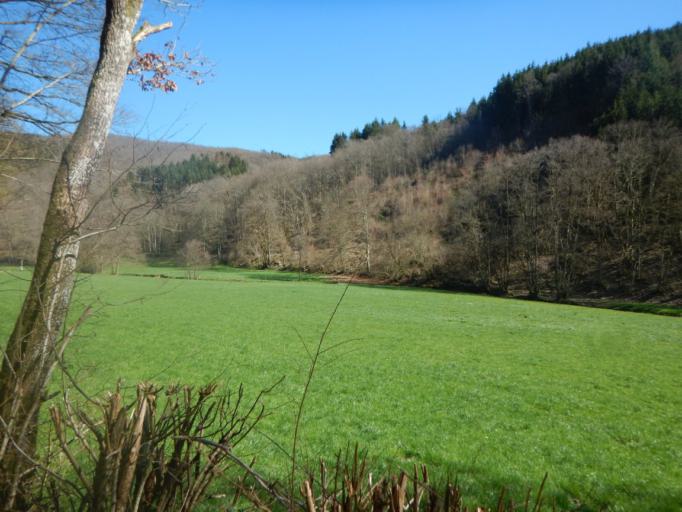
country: LU
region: Diekirch
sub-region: Canton de Wiltz
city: Wilwerwiltz
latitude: 49.9688
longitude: 5.9716
